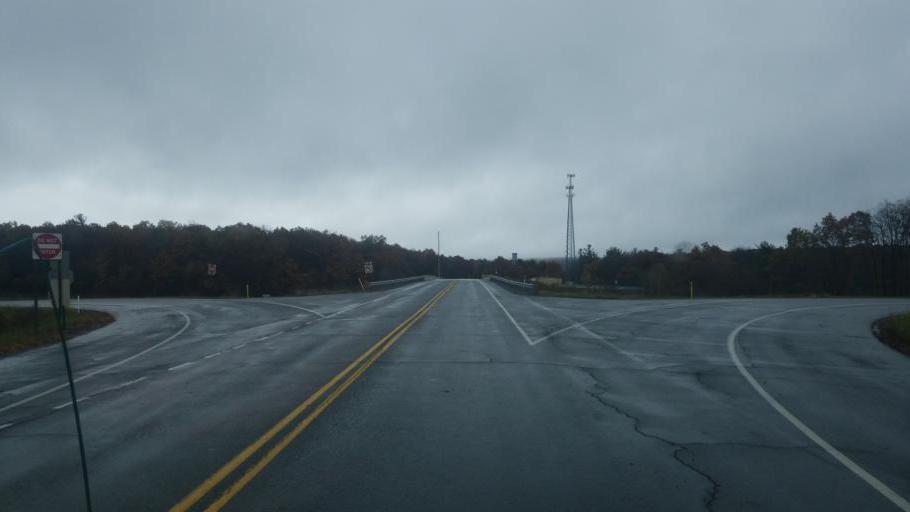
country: US
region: Pennsylvania
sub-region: Centre County
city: Milesburg
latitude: 41.0255
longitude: -77.9351
